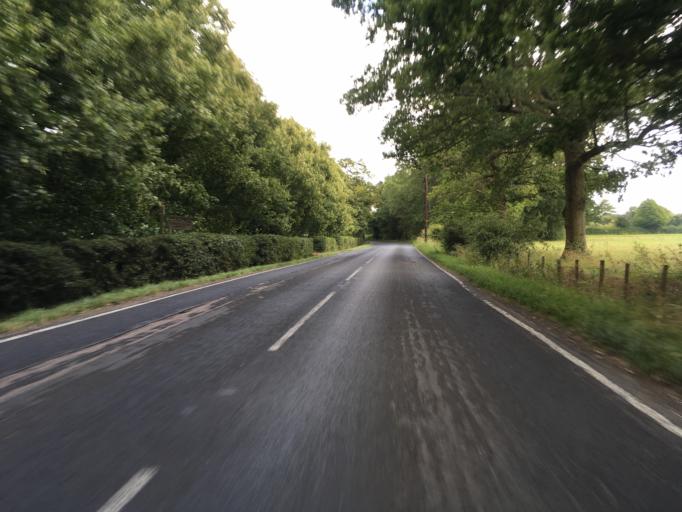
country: GB
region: England
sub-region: Kent
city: Tenterden
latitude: 51.0993
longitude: 0.6732
